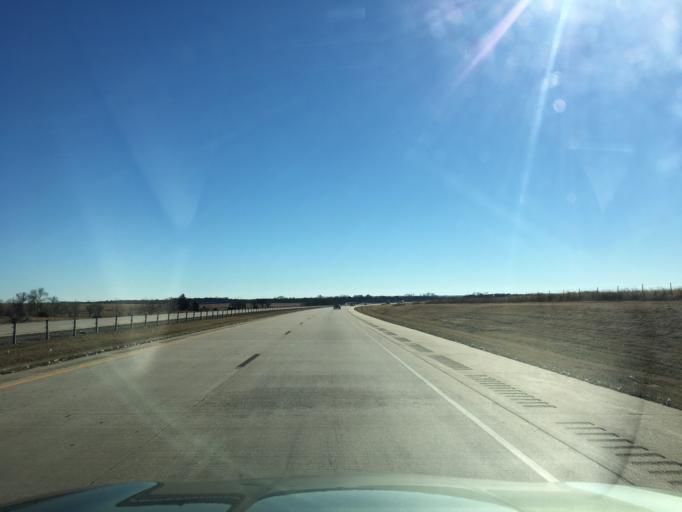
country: US
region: Oklahoma
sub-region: Kay County
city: Tonkawa
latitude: 36.4908
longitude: -97.3298
